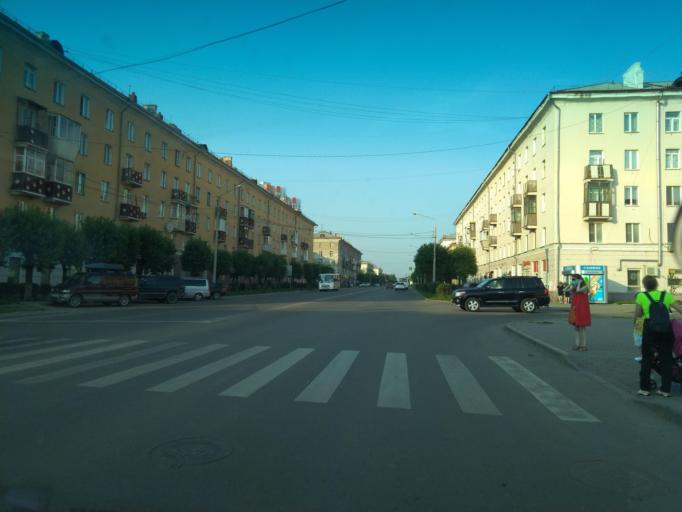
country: RU
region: Krasnoyarskiy
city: Krasnoyarsk
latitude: 55.9975
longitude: 92.9283
